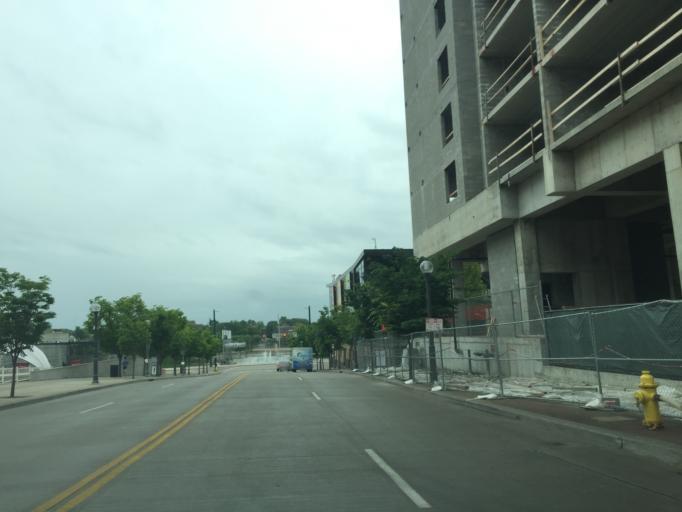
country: US
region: Kentucky
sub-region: Kenton County
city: Covington
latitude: 39.0970
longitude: -84.5086
